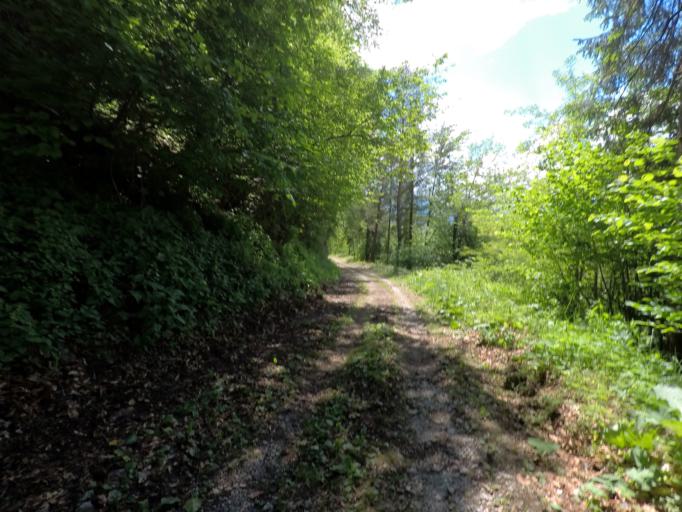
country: IT
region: Friuli Venezia Giulia
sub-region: Provincia di Udine
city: Raveo
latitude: 46.4548
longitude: 12.8766
